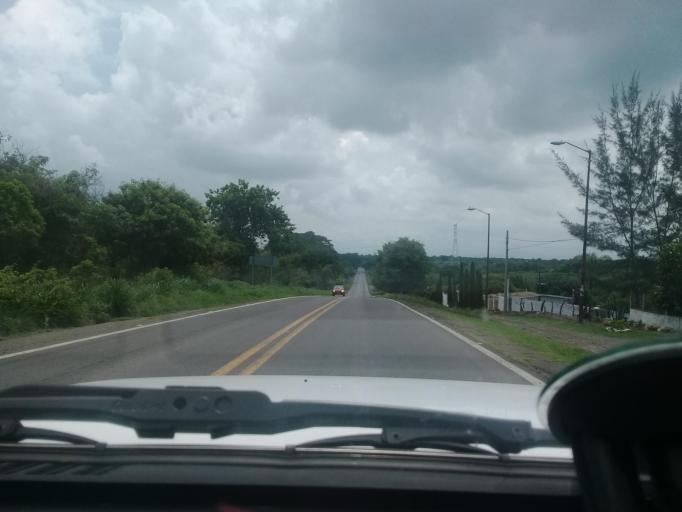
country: MX
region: Veracruz
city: Paso de Ovejas
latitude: 19.2909
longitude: -96.4491
